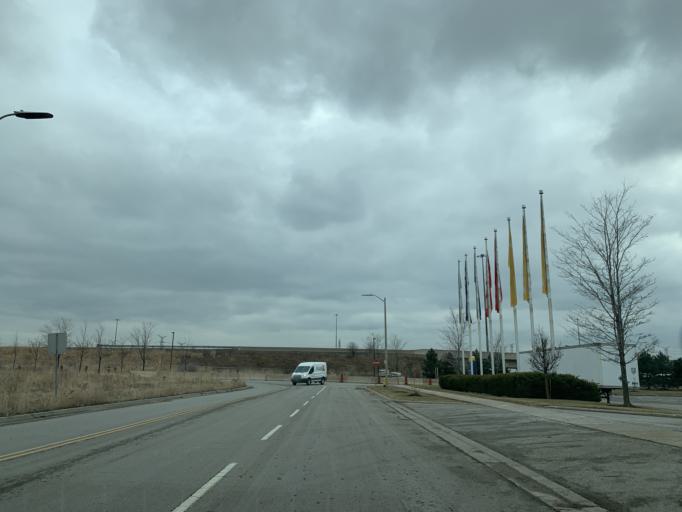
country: CA
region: Ontario
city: Concord
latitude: 43.7874
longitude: -79.5280
